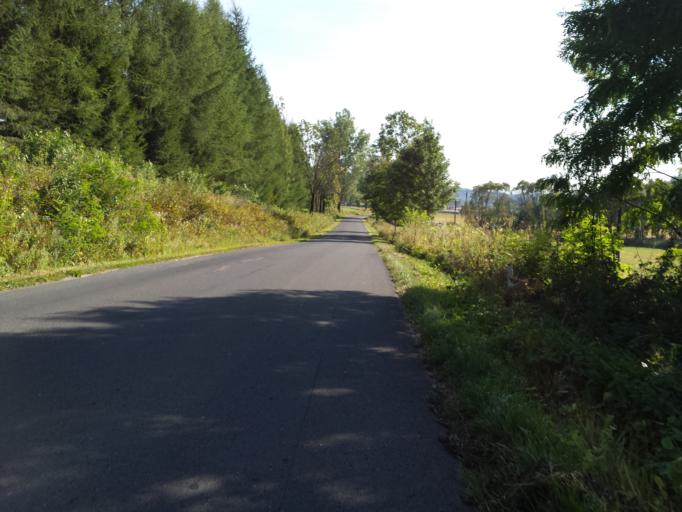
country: PL
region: Subcarpathian Voivodeship
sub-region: Powiat leski
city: Olszanica
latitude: 49.4998
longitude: 22.4507
